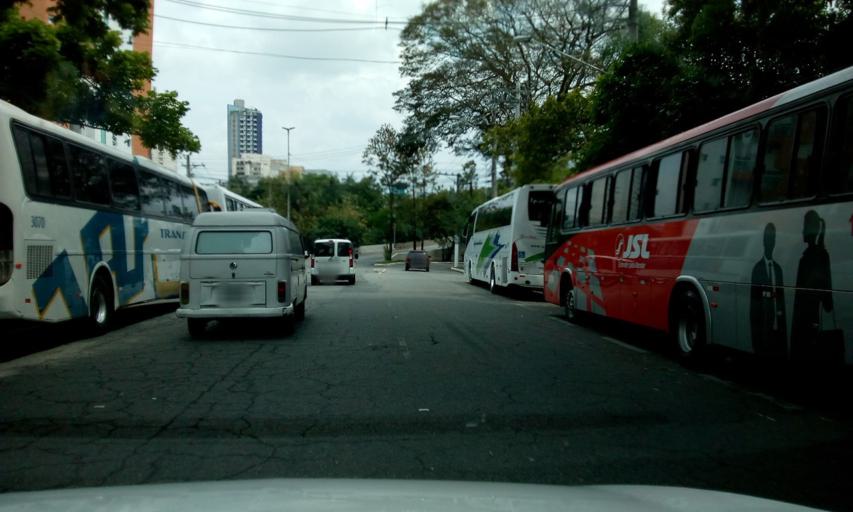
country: BR
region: Sao Paulo
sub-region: Sao Paulo
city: Sao Paulo
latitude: -23.5898
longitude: -46.6491
